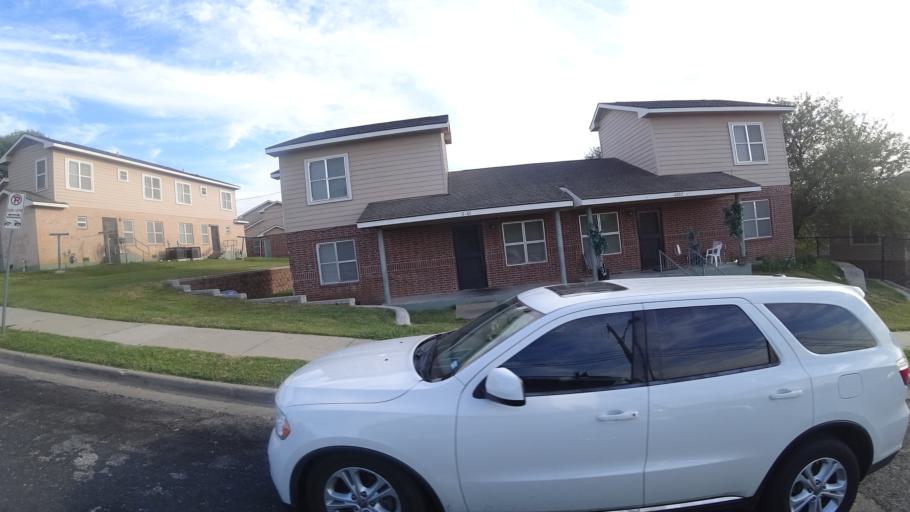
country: US
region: Texas
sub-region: Travis County
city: Austin
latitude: 30.2694
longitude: -97.7074
